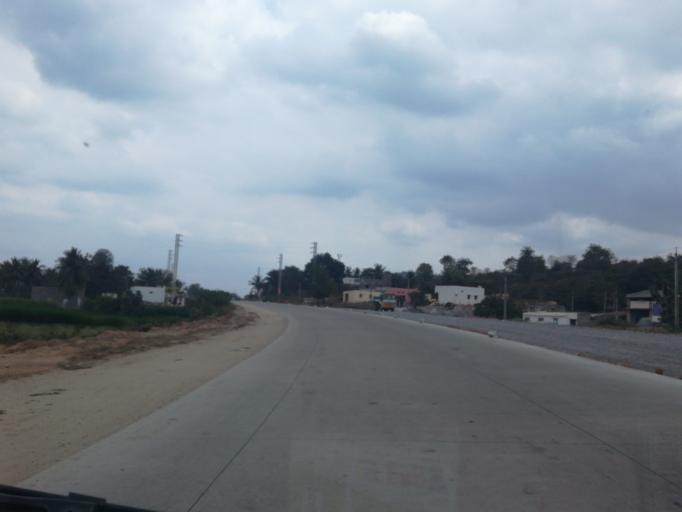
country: IN
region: Andhra Pradesh
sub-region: Chittoor
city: Ramapuram
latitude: 13.0959
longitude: 79.1275
